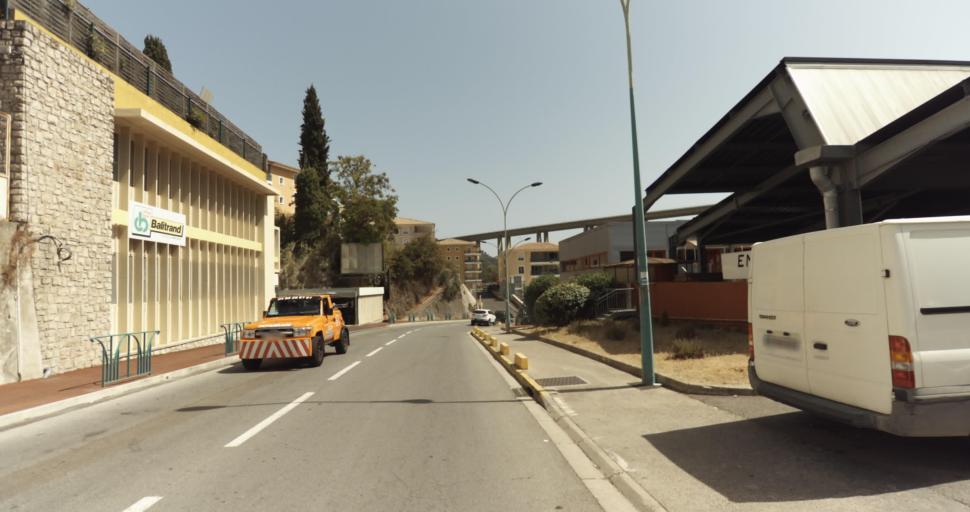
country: FR
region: Provence-Alpes-Cote d'Azur
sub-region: Departement des Alpes-Maritimes
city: Sainte-Agnes
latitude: 43.8005
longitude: 7.4882
